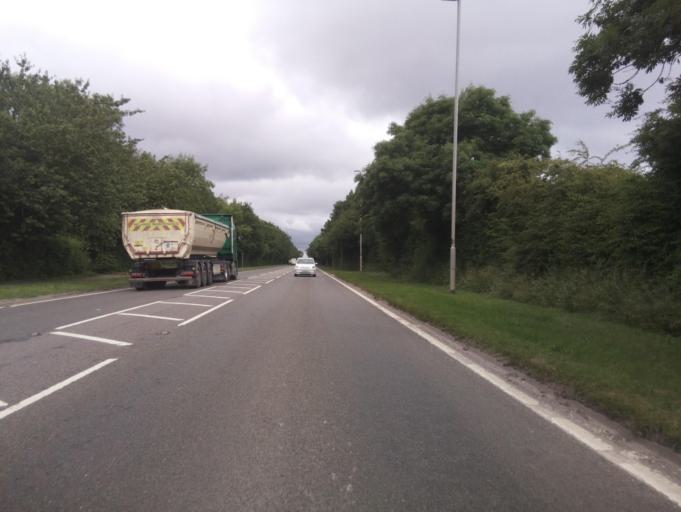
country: GB
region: England
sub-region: Leicestershire
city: Coalville
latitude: 52.7267
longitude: -1.3594
